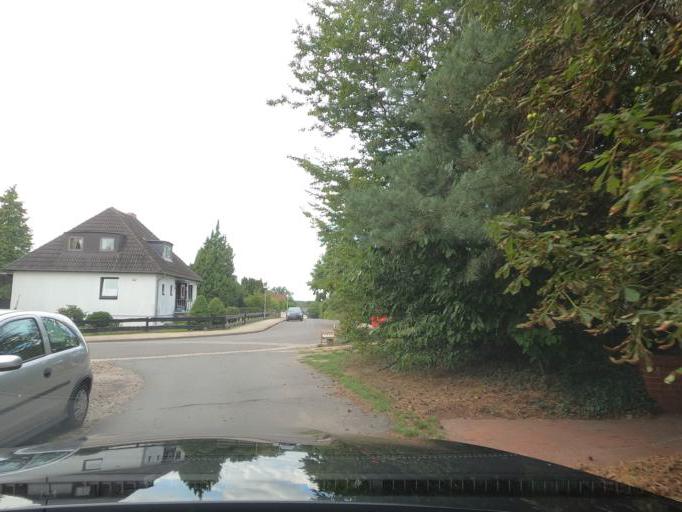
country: DE
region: Lower Saxony
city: Isernhagen Farster Bauerschaft
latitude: 52.5166
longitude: 9.9240
